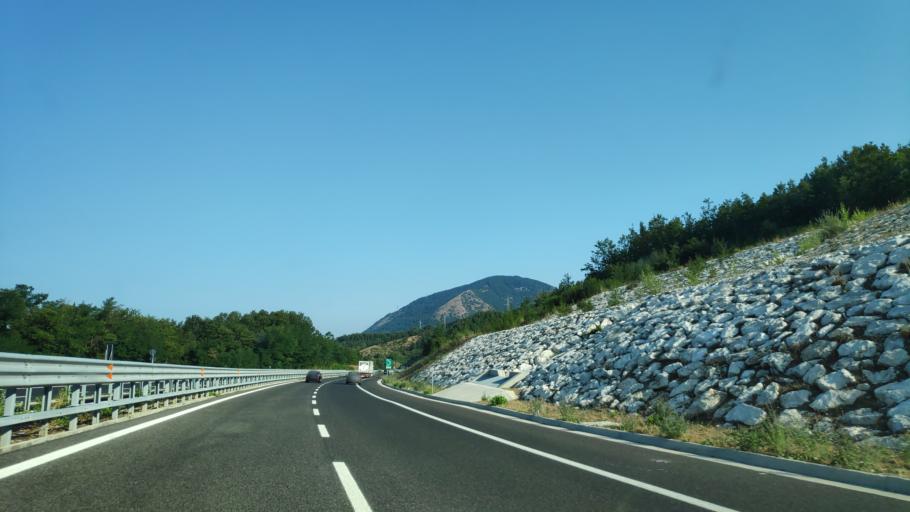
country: IT
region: Basilicate
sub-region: Provincia di Potenza
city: Nemoli
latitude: 40.1037
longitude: 15.7968
